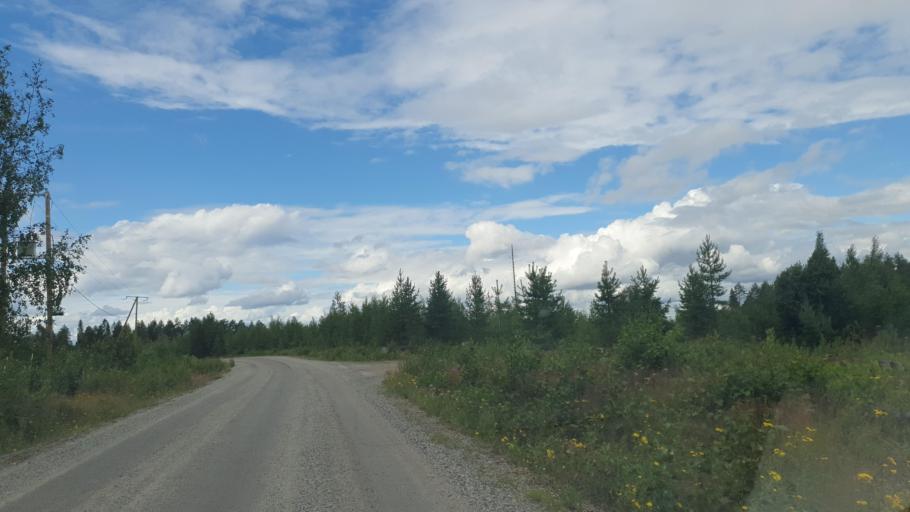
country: FI
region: Kainuu
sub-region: Kehys-Kainuu
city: Kuhmo
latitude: 64.1106
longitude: 29.3771
